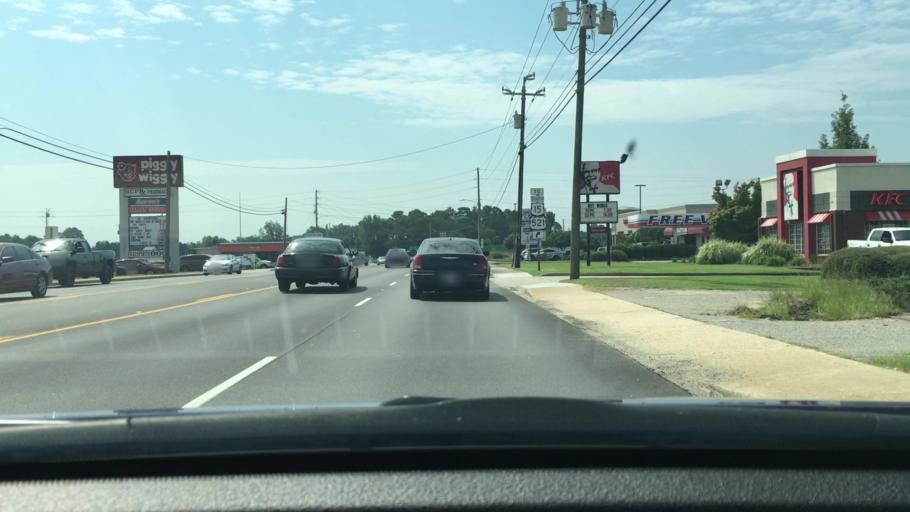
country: US
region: South Carolina
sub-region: Sumter County
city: Sumter
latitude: 33.9467
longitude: -80.3738
